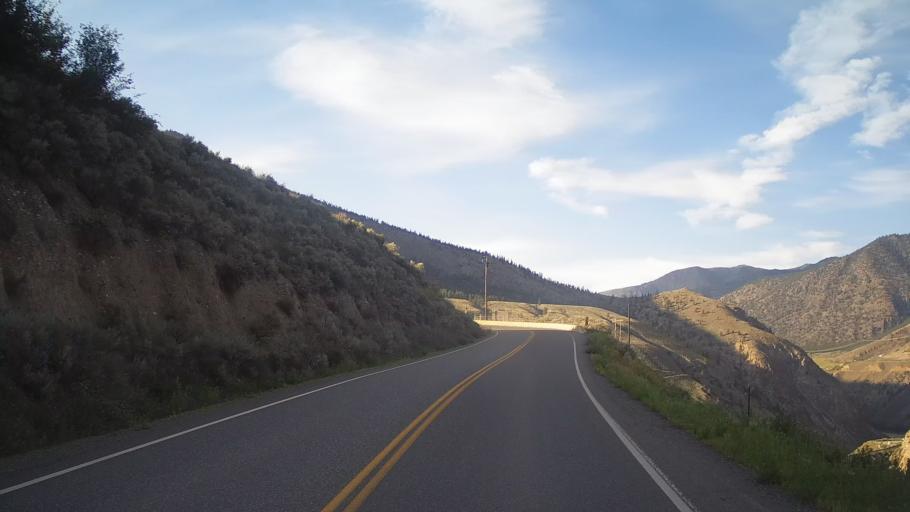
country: CA
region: British Columbia
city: Lillooet
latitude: 50.7411
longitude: -121.8624
